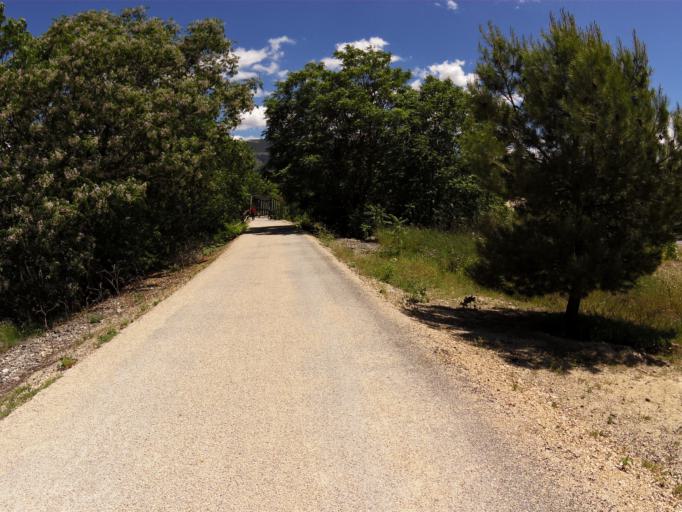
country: ES
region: Andalusia
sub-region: Provincia de Jaen
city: Torredonjimeno
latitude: 37.7547
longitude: -3.9564
